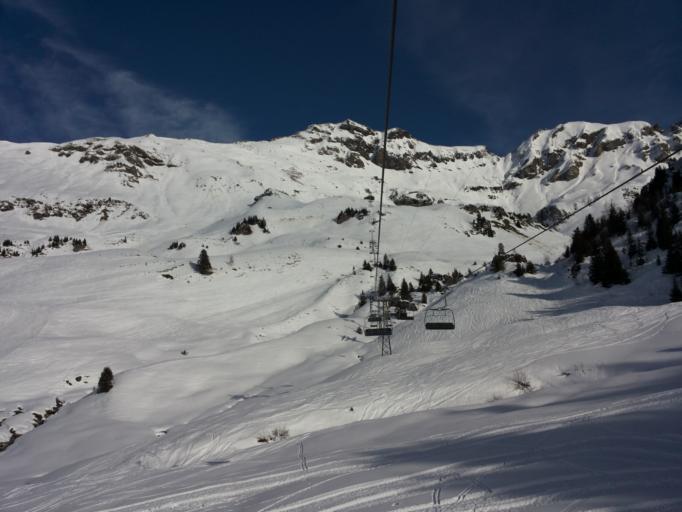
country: CH
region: Bern
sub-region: Interlaken-Oberhasli District
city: Meiringen
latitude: 46.7509
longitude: 8.2423
